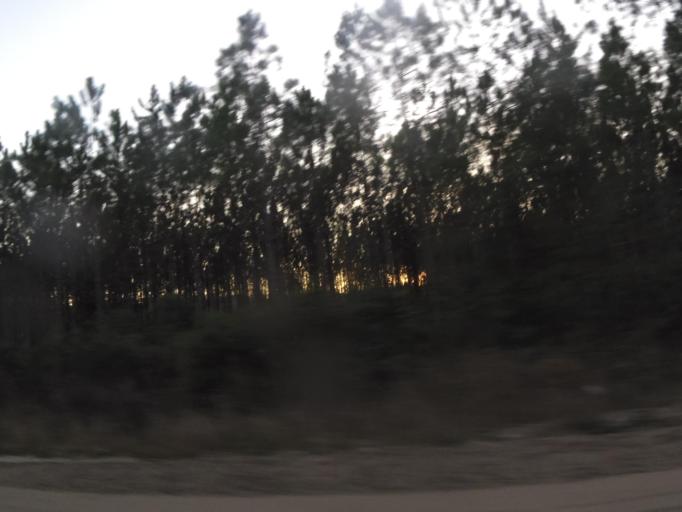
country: US
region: Florida
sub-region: Clay County
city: Asbury Lake
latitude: 29.9403
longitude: -81.7861
